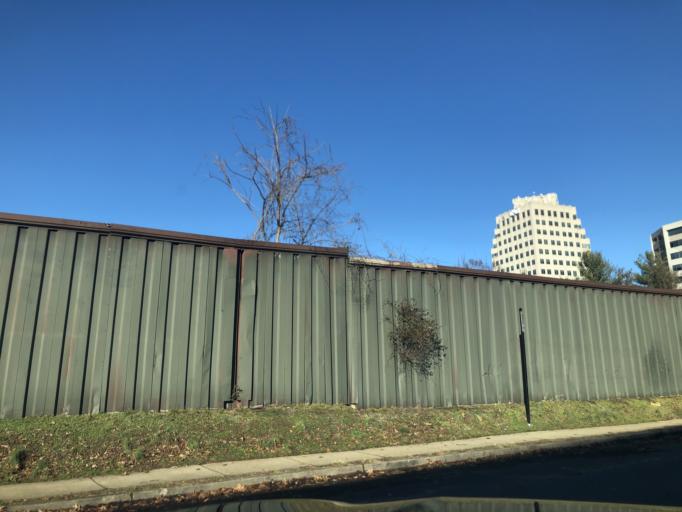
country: US
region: Virginia
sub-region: Arlington County
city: Arlington
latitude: 38.8818
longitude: -77.1199
